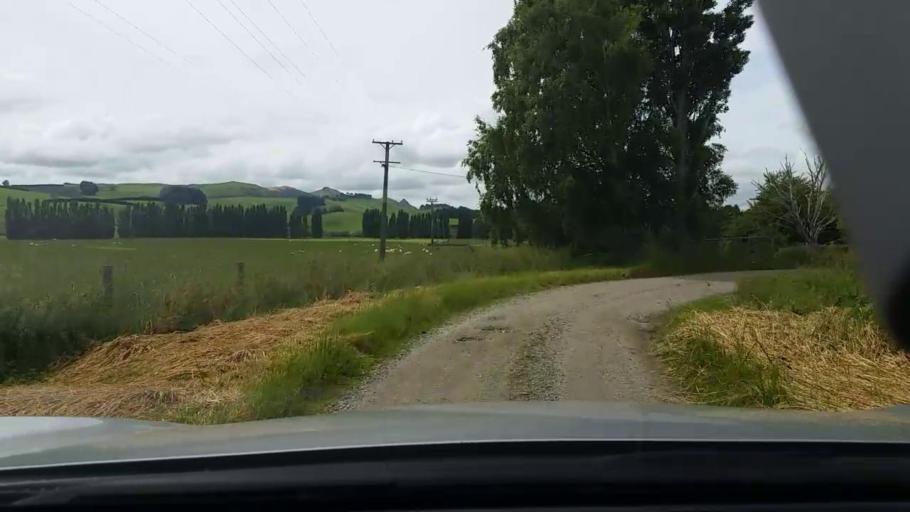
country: NZ
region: Southland
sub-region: Gore District
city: Gore
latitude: -46.1242
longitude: 168.9314
